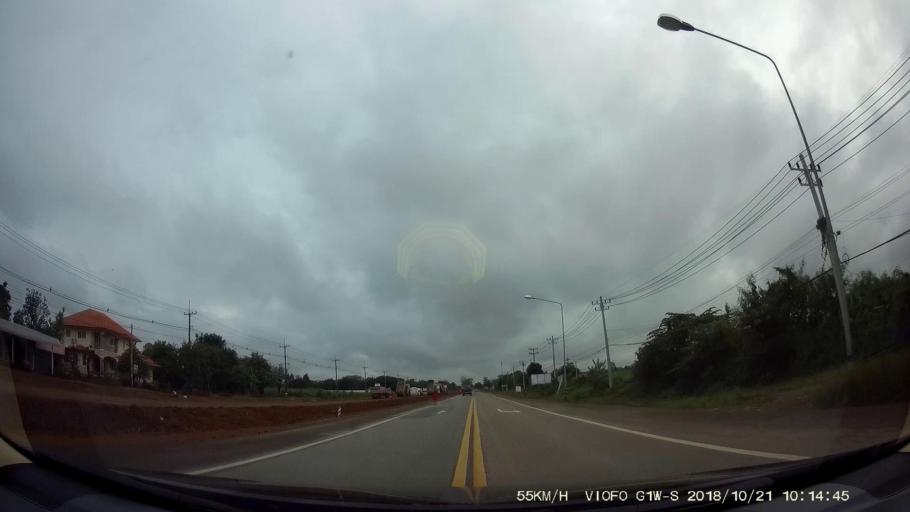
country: TH
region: Chaiyaphum
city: Phu Khiao
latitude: 16.3462
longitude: 102.1594
